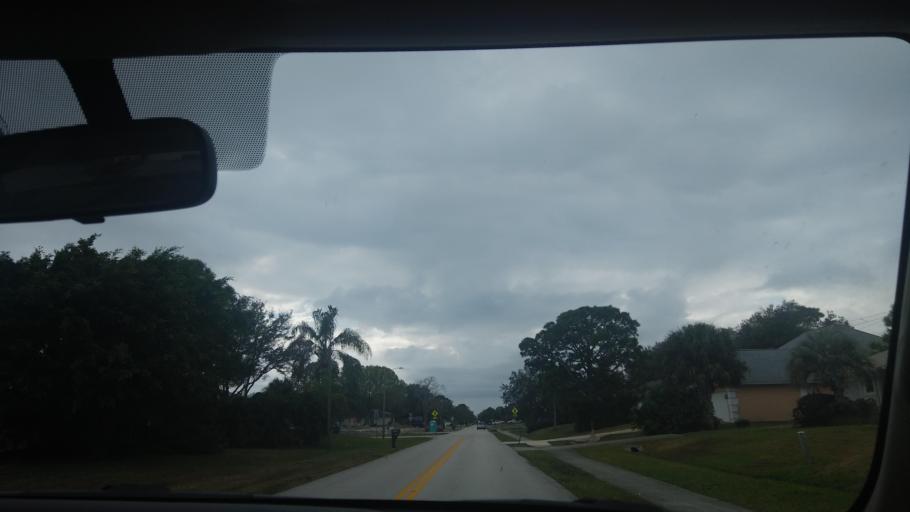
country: US
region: Florida
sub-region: Indian River County
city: Sebastian
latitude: 27.8080
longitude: -80.4879
